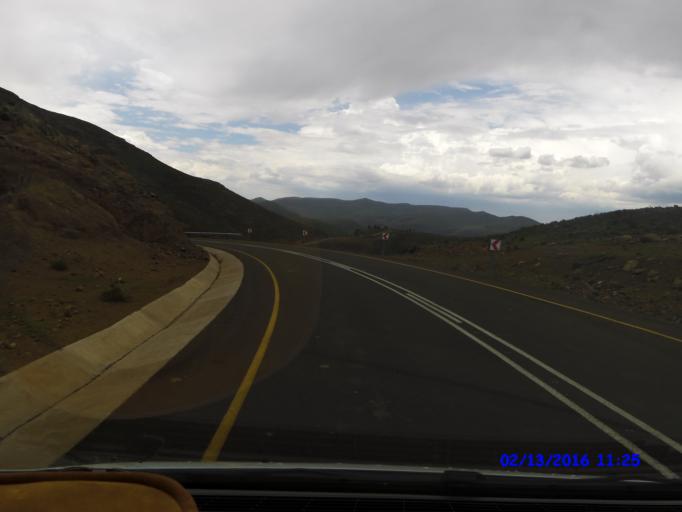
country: LS
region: Maseru
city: Nako
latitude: -29.7670
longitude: 28.0052
